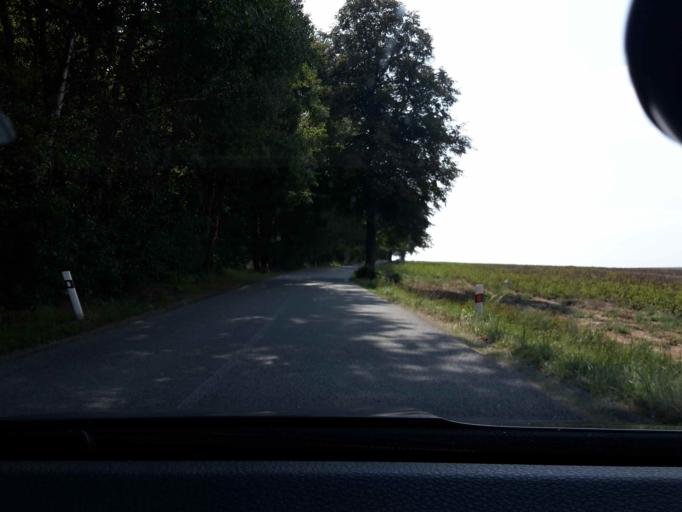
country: CZ
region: Vysocina
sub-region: Okres Jihlava
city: Trest'
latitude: 49.2612
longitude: 15.5716
